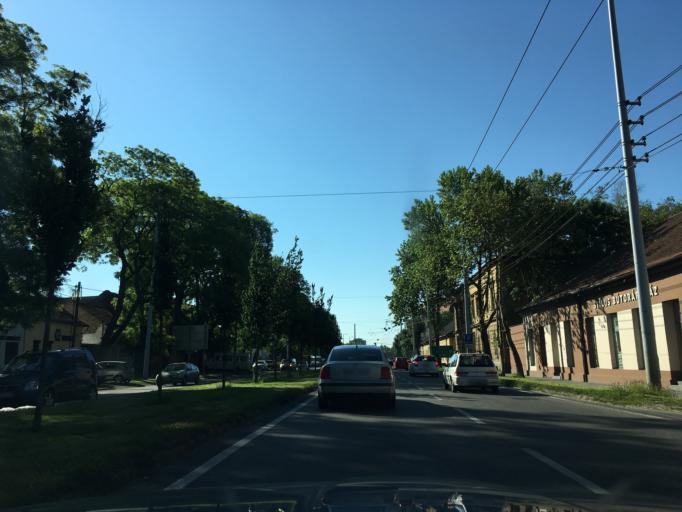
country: HU
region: Hajdu-Bihar
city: Debrecen
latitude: 47.5274
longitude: 21.6153
